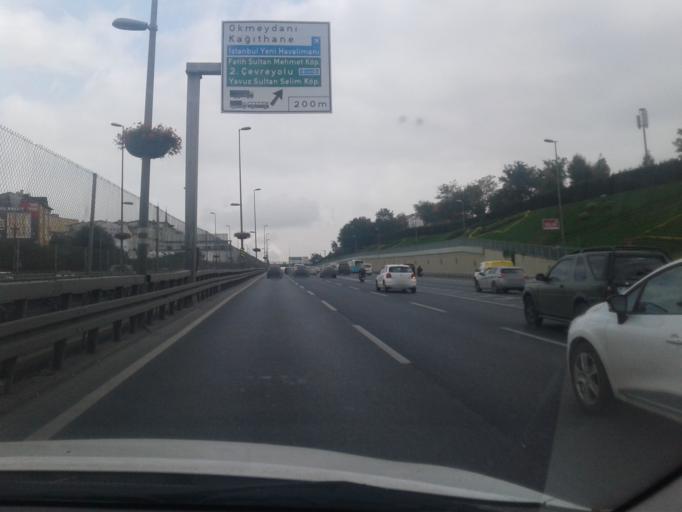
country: TR
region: Istanbul
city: Sisli
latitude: 41.0523
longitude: 28.9525
